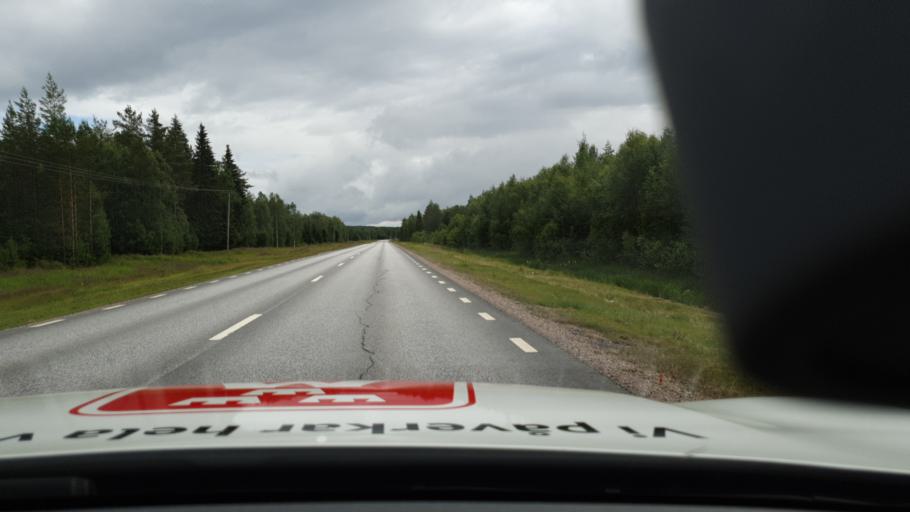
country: SE
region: Norrbotten
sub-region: Pitea Kommun
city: Rosvik
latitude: 65.5770
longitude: 21.7183
